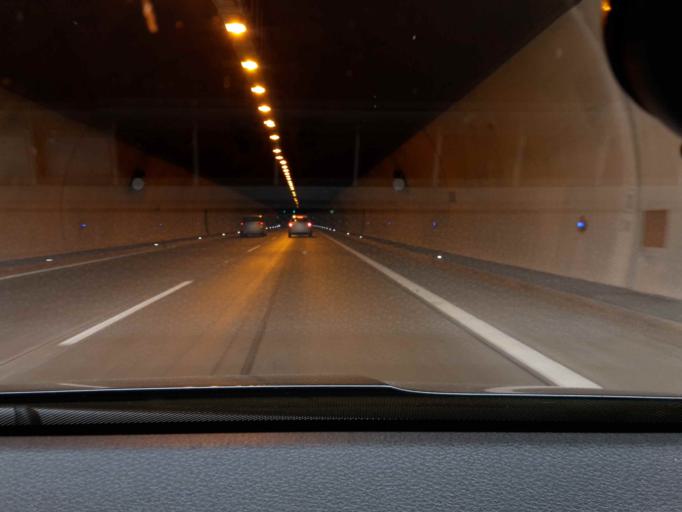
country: CZ
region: Central Bohemia
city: Dolni Brezany
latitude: 49.9822
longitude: 14.4323
